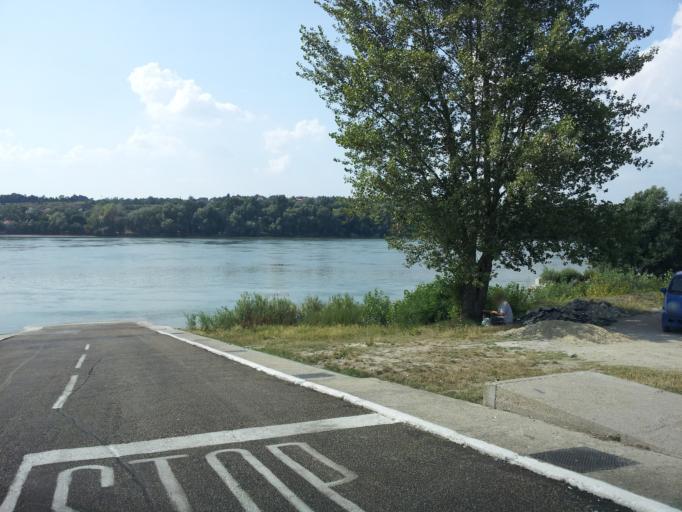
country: HU
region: Pest
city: Toekoel
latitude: 47.3284
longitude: 18.9502
